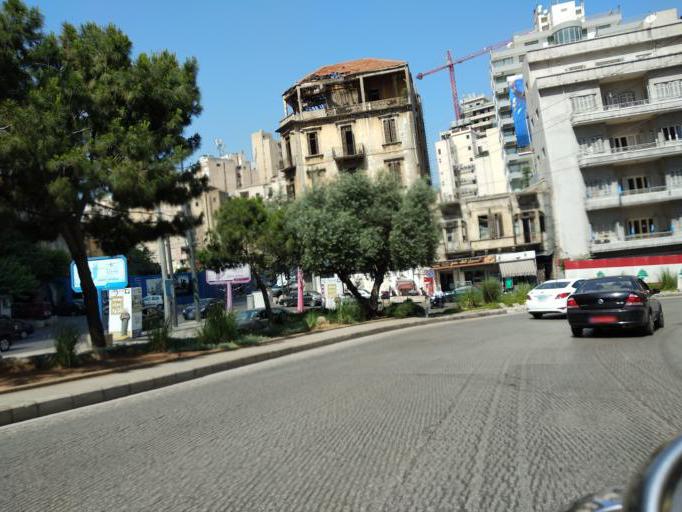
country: LB
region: Beyrouth
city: Beirut
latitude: 33.8950
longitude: 35.4964
